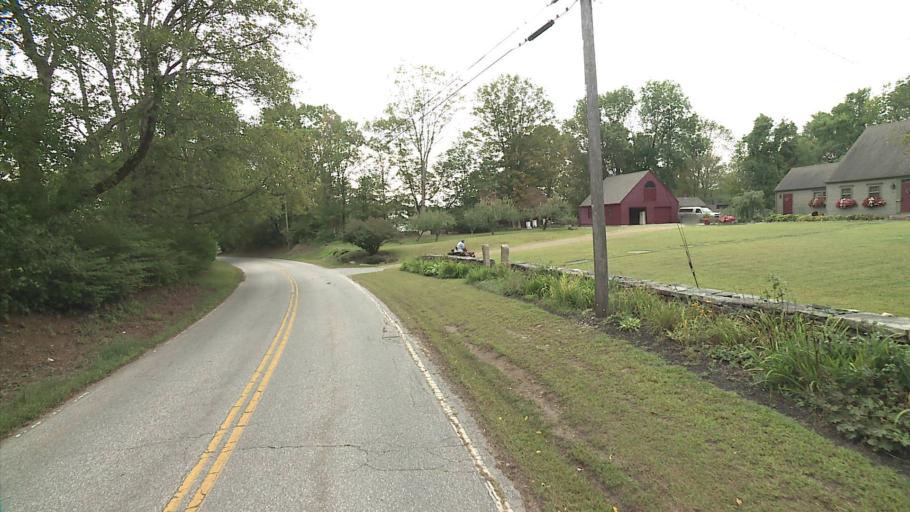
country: US
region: Connecticut
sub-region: Windham County
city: Wauregan
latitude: 41.7225
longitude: -71.9152
